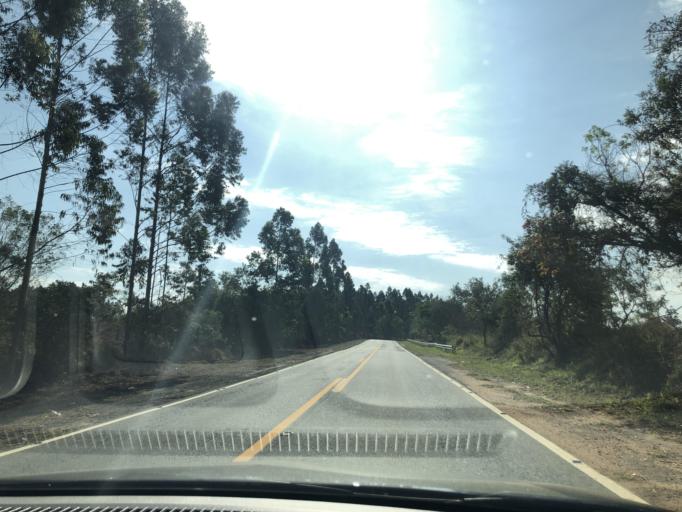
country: BR
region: Sao Paulo
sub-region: Pilar Do Sul
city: Pilar do Sul
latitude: -23.8251
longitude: -47.6796
